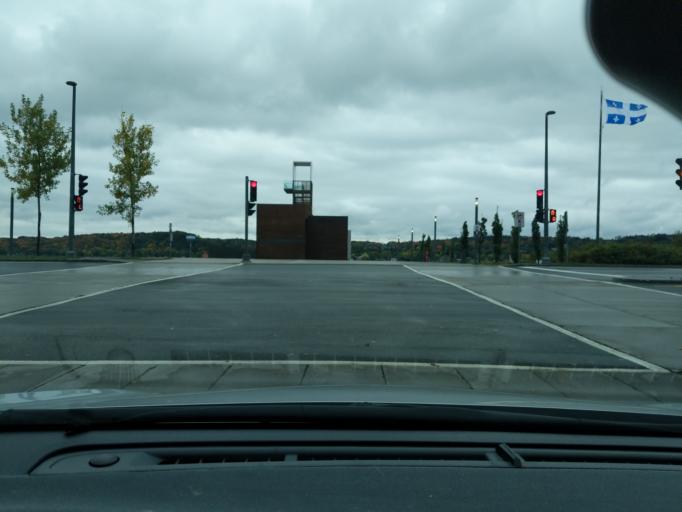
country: CA
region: Quebec
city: Quebec
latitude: 46.7559
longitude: -71.2726
